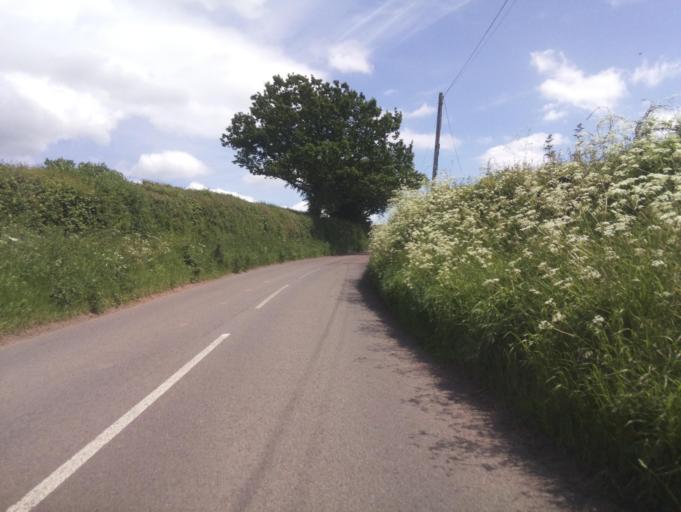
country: GB
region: England
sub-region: Herefordshire
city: Llanrothal
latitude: 51.8415
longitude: -2.7742
